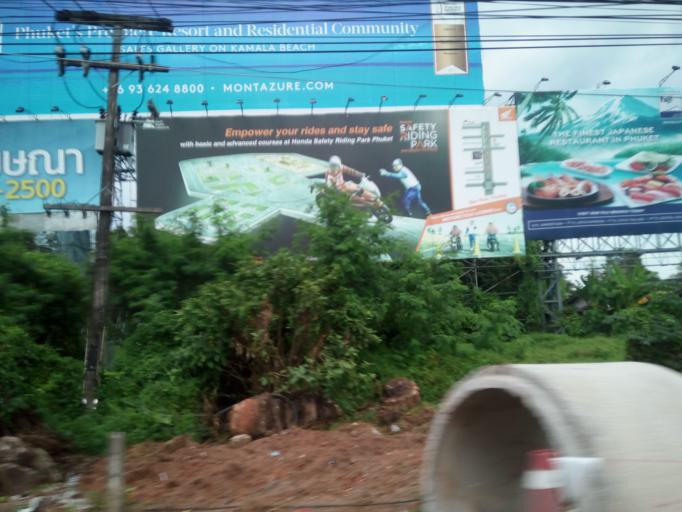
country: TH
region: Phuket
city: Thalang
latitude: 8.0933
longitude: 98.3385
